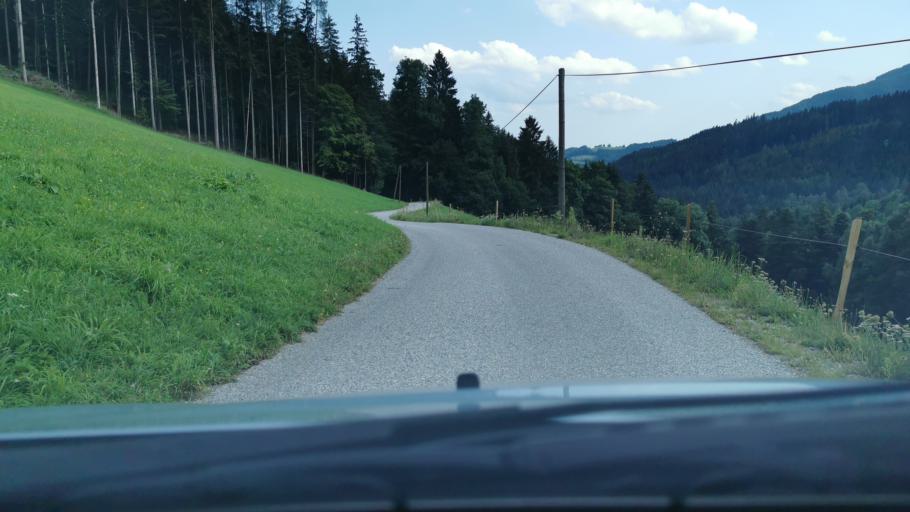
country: AT
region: Styria
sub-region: Politischer Bezirk Weiz
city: Koglhof
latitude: 47.3242
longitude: 15.6651
